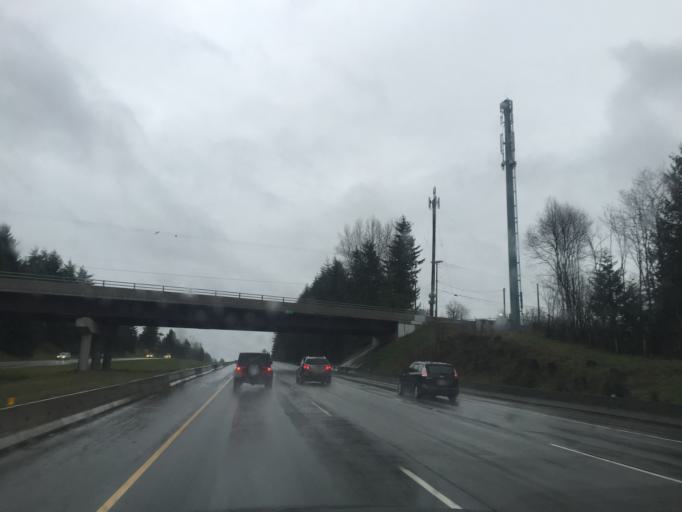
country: CA
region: British Columbia
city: Langley
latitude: 49.1193
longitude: -122.5383
